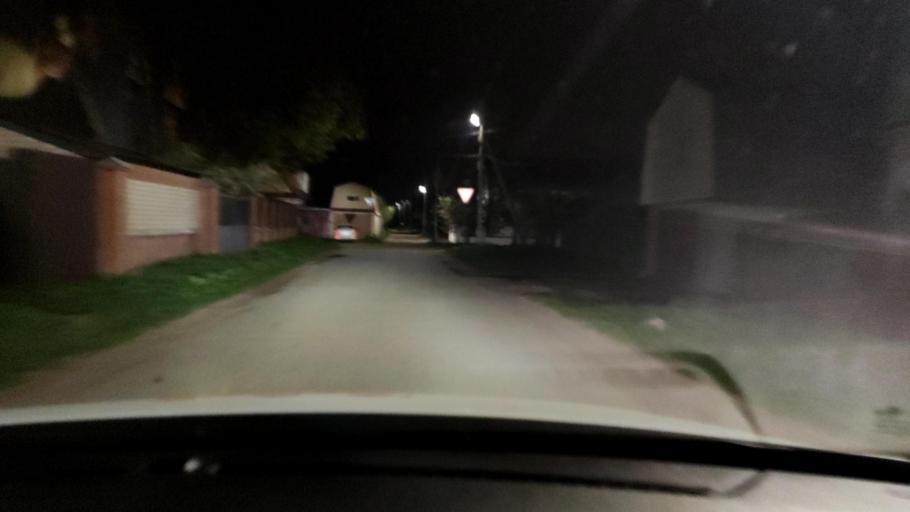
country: RU
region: Tatarstan
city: Stolbishchi
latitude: 55.7043
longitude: 49.1494
